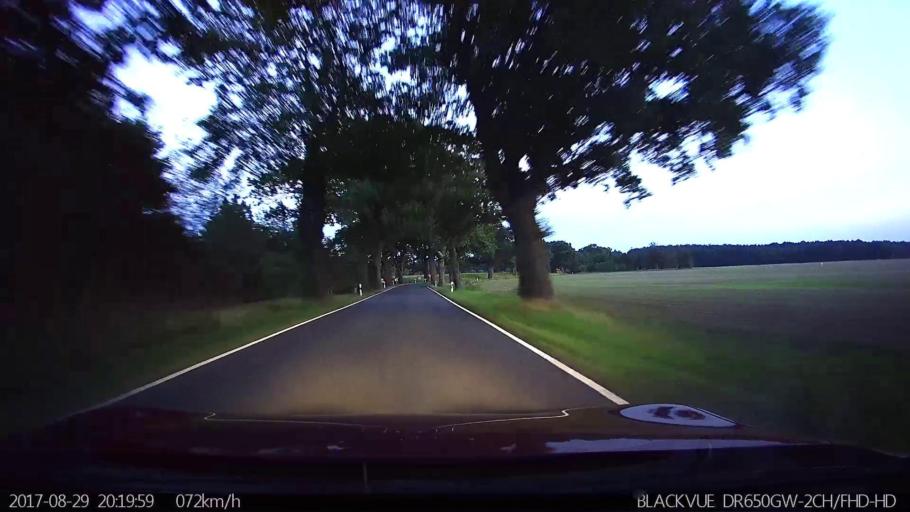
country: DE
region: Mecklenburg-Vorpommern
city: Velgast
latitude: 54.2636
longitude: 12.8190
